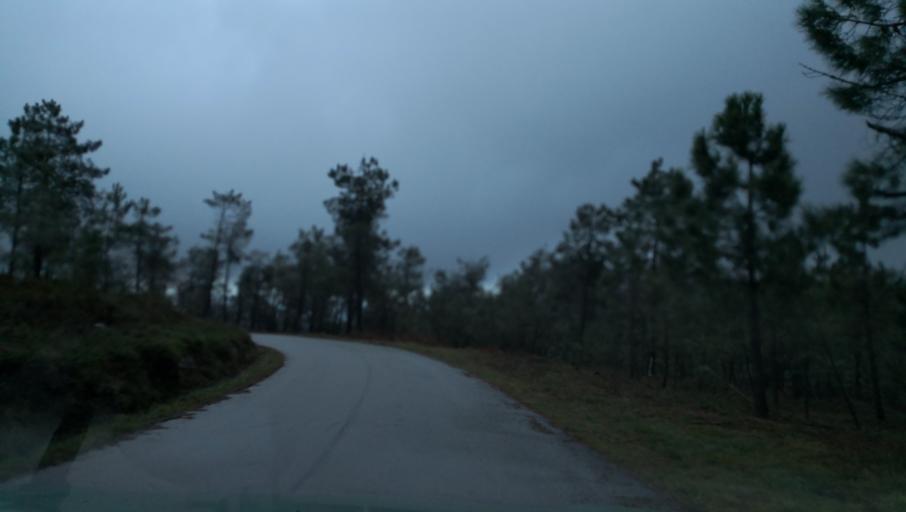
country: PT
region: Vila Real
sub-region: Santa Marta de Penaguiao
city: Santa Marta de Penaguiao
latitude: 41.2886
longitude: -7.8983
